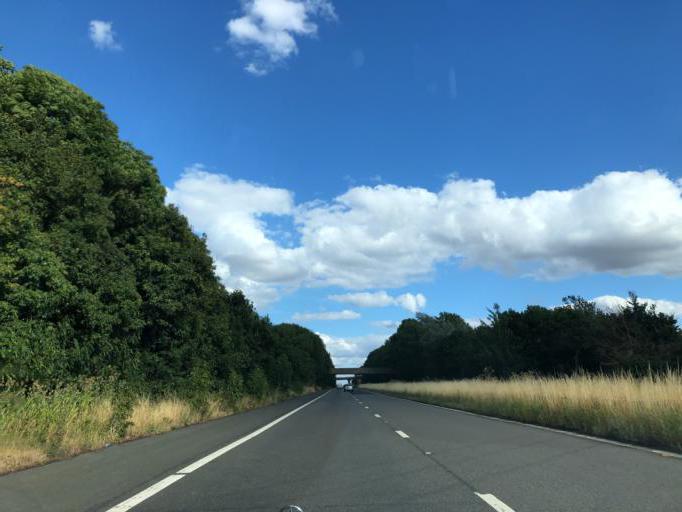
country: GB
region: England
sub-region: Northamptonshire
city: Daventry
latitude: 52.3322
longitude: -1.1827
